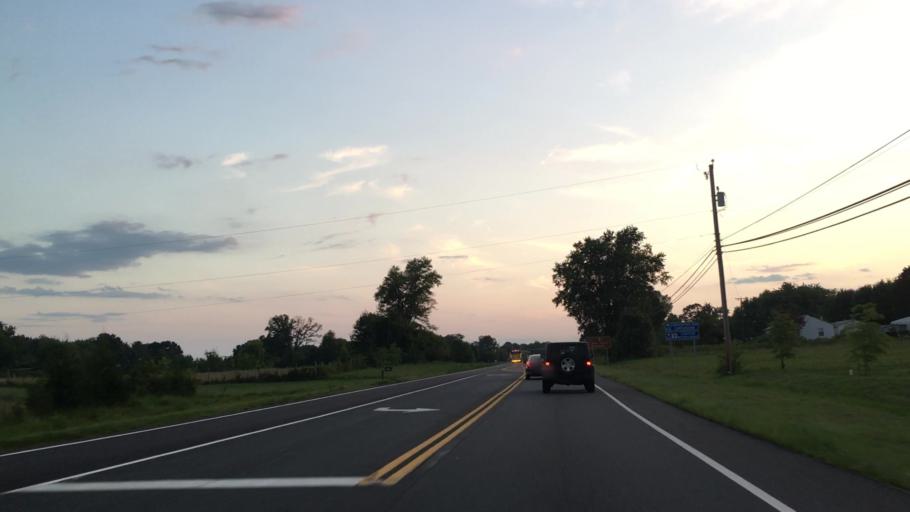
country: US
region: Virginia
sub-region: Orange County
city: Orange
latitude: 38.2675
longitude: -77.9521
